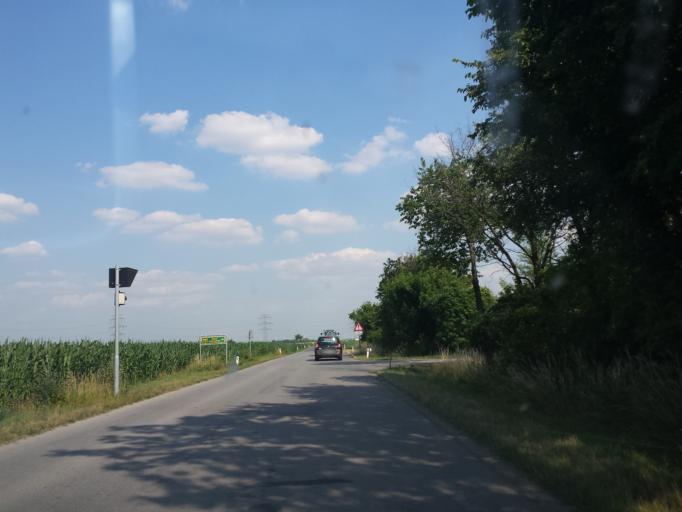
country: AT
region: Lower Austria
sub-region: Politischer Bezirk Ganserndorf
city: Aderklaa
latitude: 48.2826
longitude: 16.5485
